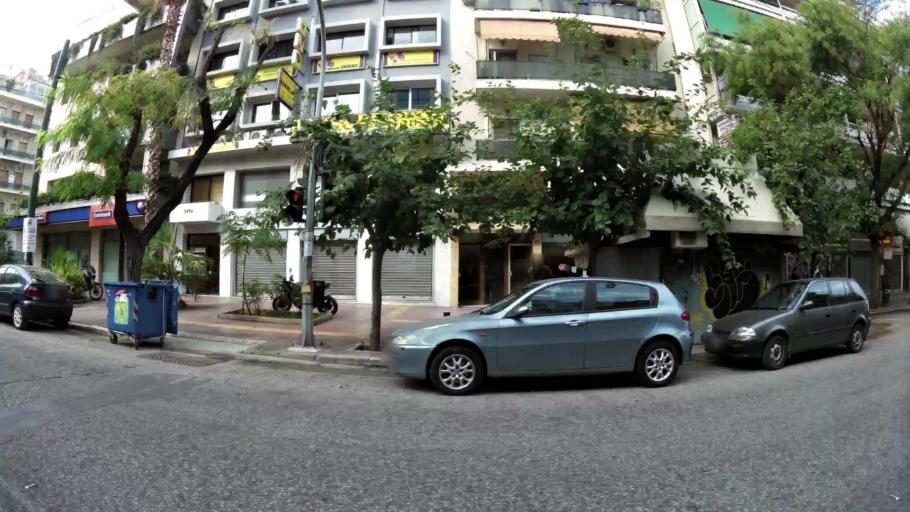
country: GR
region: Attica
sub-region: Nomarchia Athinas
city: Nea Chalkidona
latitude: 38.0224
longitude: 23.7358
